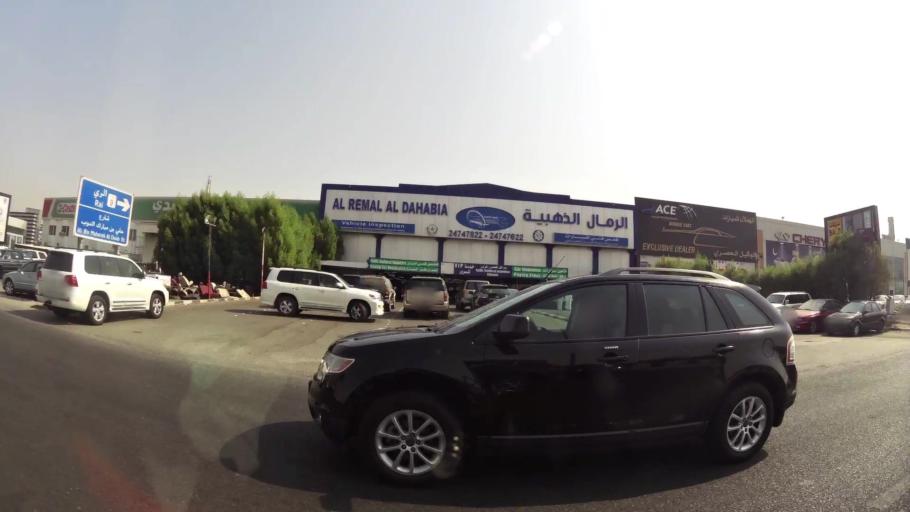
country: KW
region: Al Asimah
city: Ar Rabiyah
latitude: 29.3071
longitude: 47.9270
